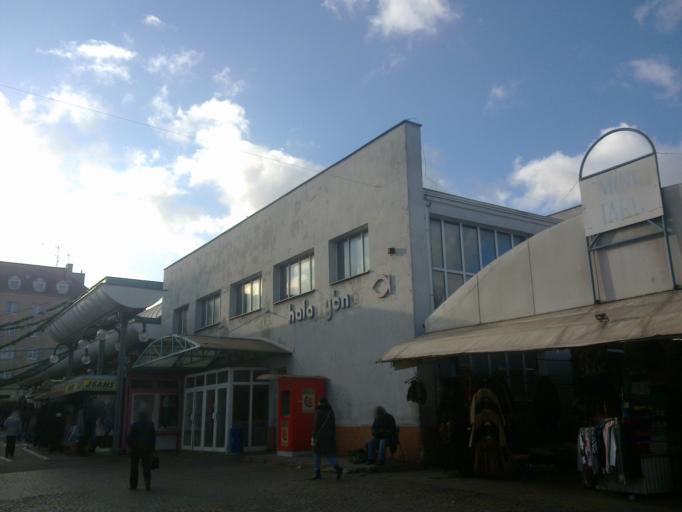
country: PL
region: Pomeranian Voivodeship
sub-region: Gdynia
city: Gdynia
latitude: 54.5229
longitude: 18.5330
